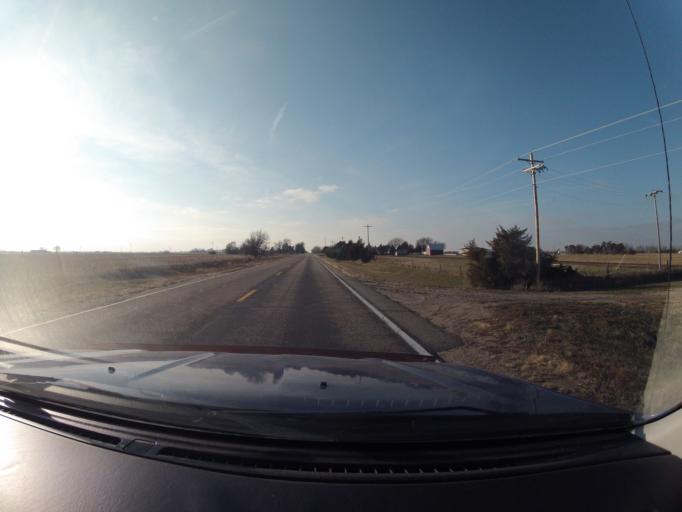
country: US
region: Nebraska
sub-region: Buffalo County
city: Kearney
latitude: 40.6410
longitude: -99.0798
